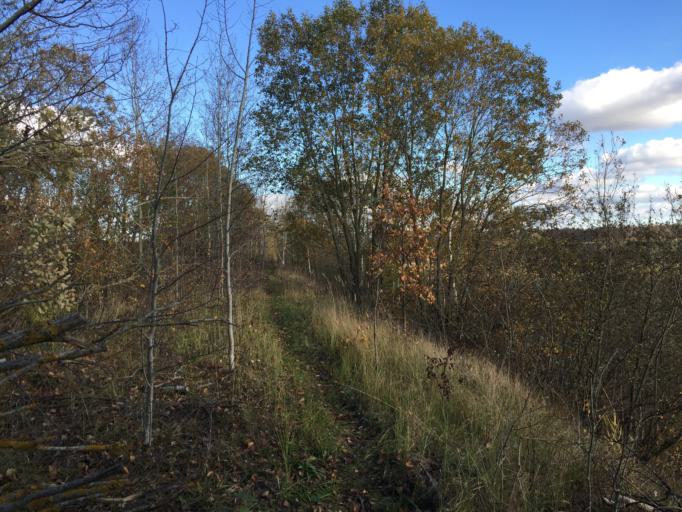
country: LV
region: Tukuma Rajons
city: Tukums
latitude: 56.9583
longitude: 23.0861
